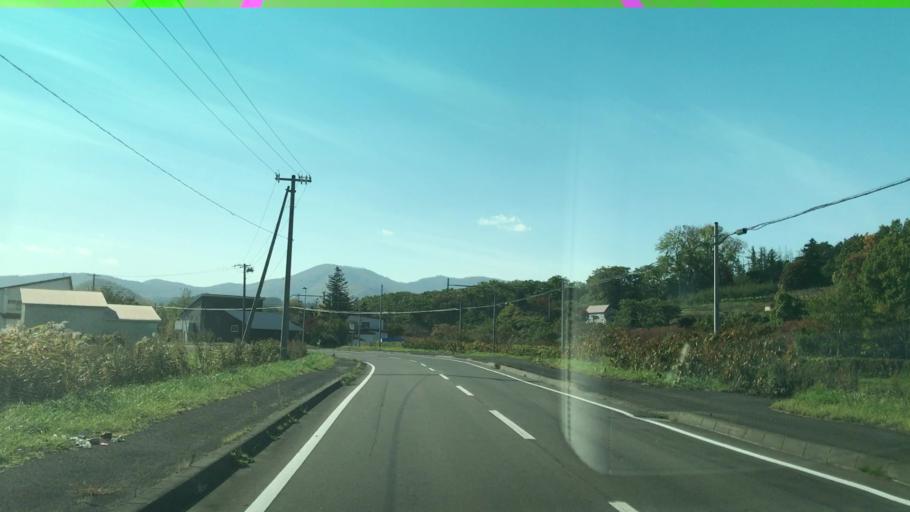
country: JP
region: Hokkaido
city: Yoichi
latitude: 43.1697
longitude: 140.8209
